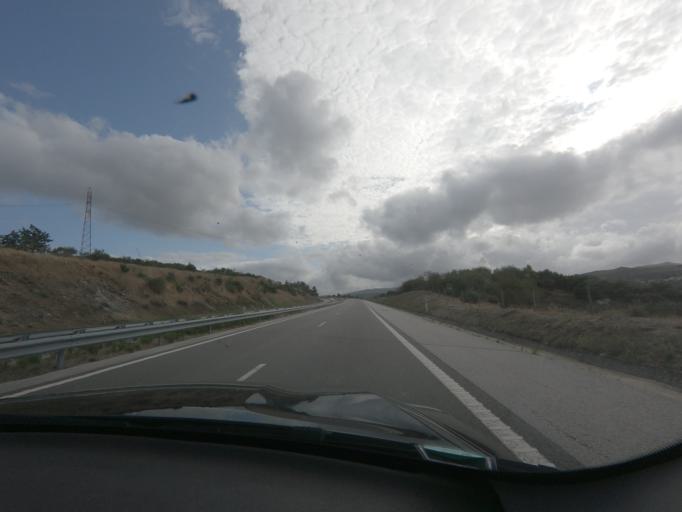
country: PT
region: Viseu
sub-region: Tarouca
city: Tarouca
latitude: 41.0200
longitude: -7.8781
